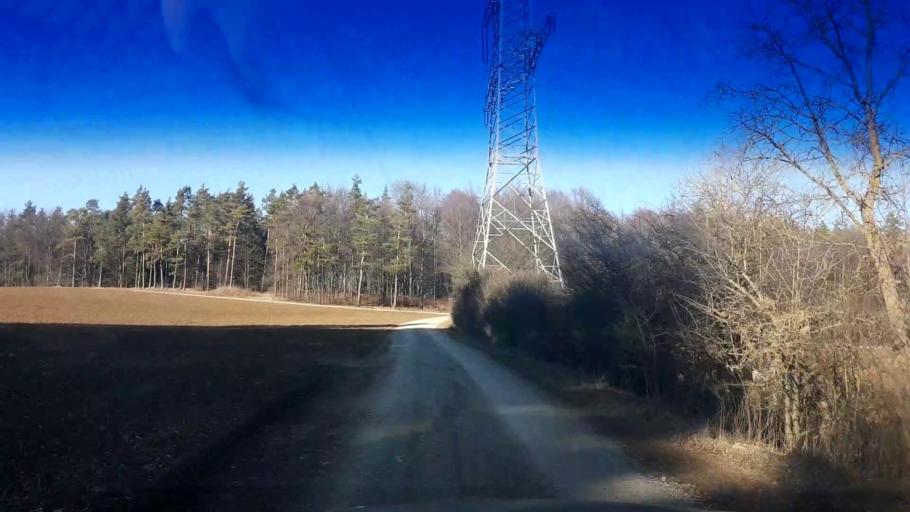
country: DE
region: Bavaria
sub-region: Upper Franconia
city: Poxdorf
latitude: 49.9657
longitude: 11.0857
